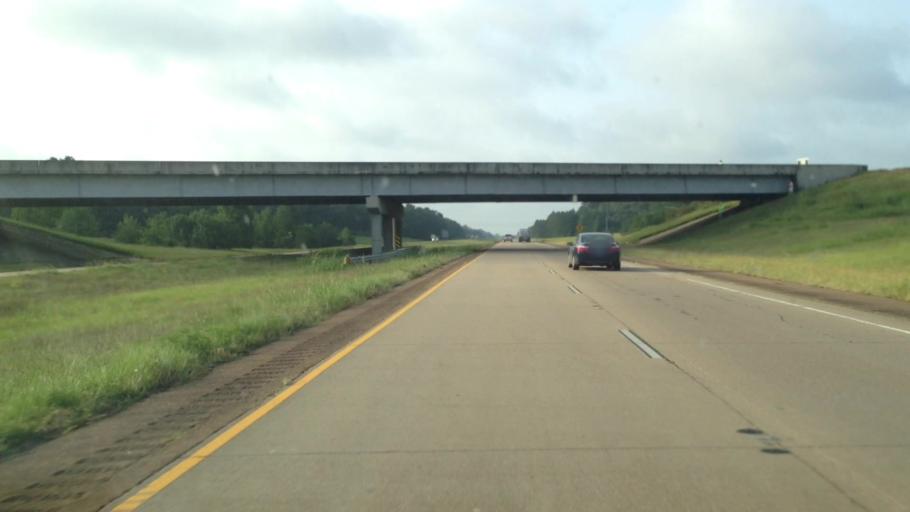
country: US
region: Louisiana
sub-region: Rapides Parish
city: Lecompte
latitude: 31.0724
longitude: -92.4341
